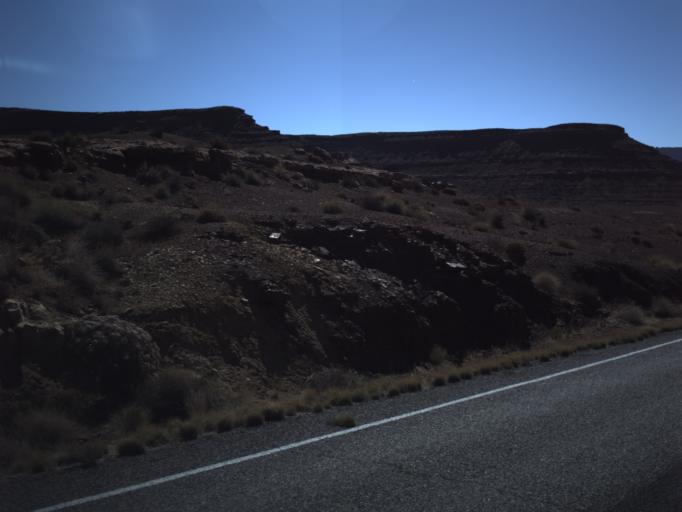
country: US
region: Utah
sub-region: San Juan County
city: Blanding
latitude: 37.8507
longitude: -110.3539
